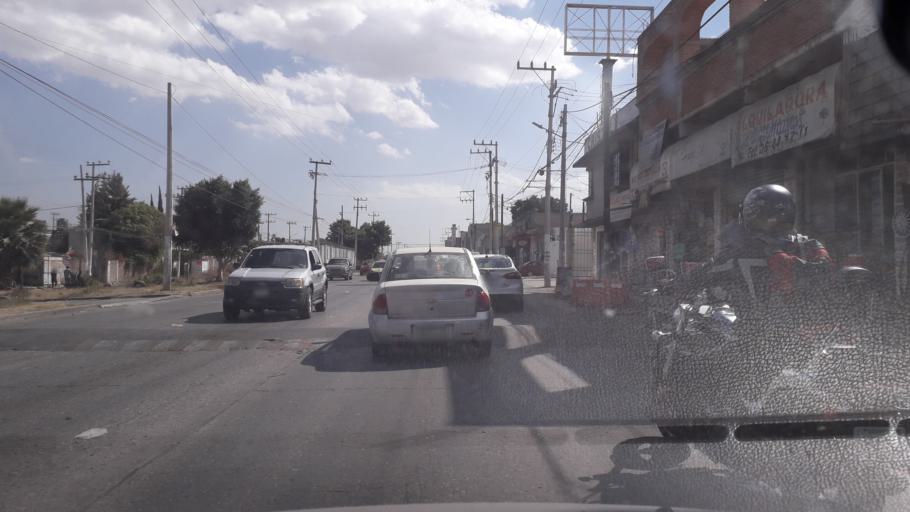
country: MX
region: Mexico
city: Ecatepec
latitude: 19.6313
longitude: -99.0526
